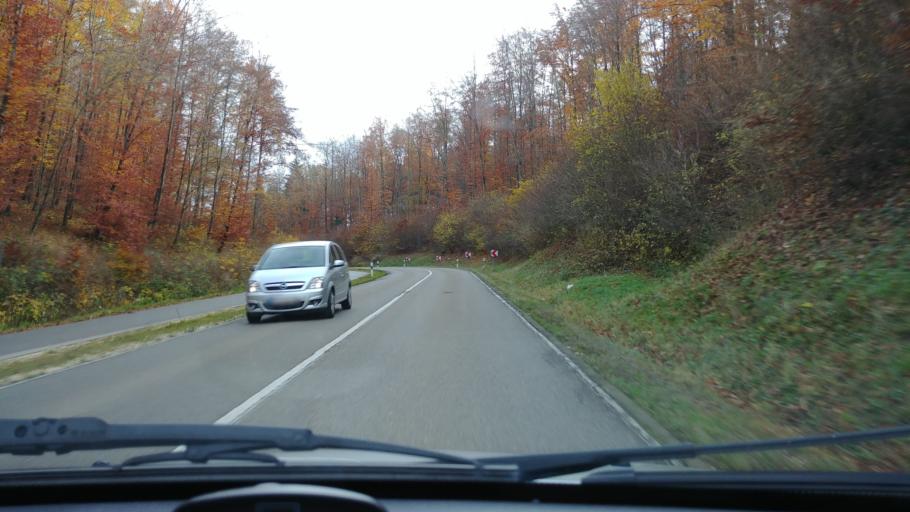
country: DE
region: Baden-Wuerttemberg
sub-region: Regierungsbezirk Stuttgart
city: Herbrechtingen
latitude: 48.6629
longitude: 10.2035
